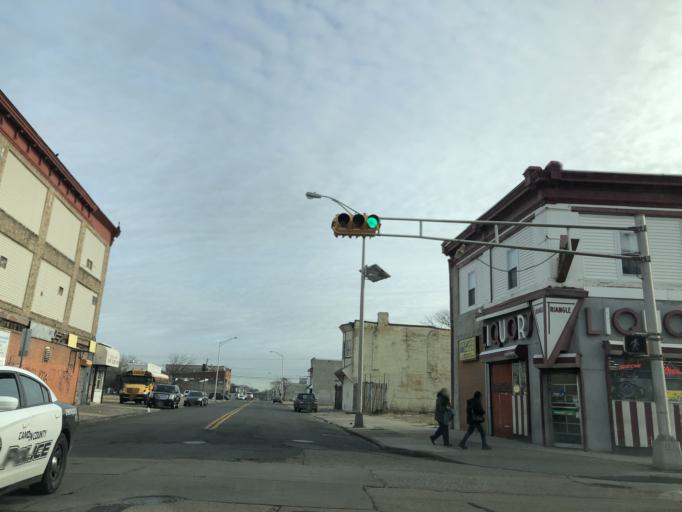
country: US
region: New Jersey
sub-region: Camden County
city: Camden
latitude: 39.9309
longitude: -75.1196
